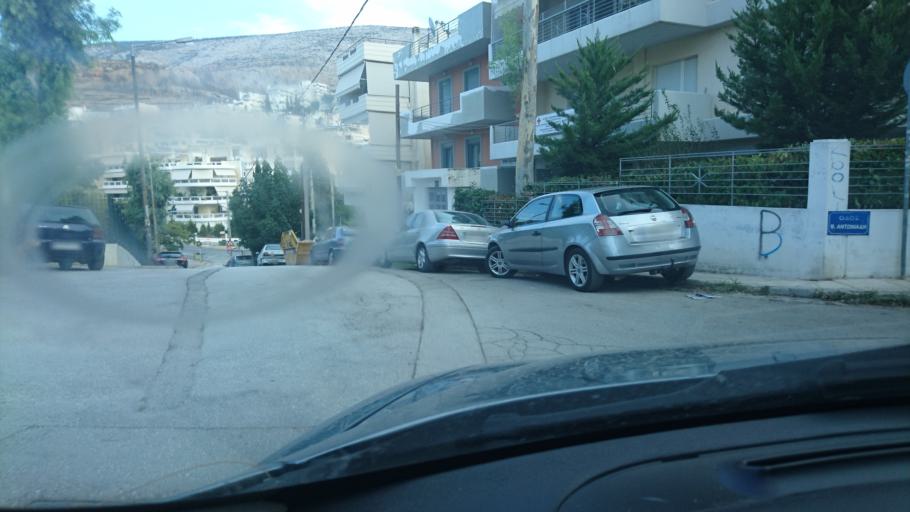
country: GR
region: Attica
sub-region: Nomarchia Athinas
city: Ilioupoli
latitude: 37.9449
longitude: 23.7685
